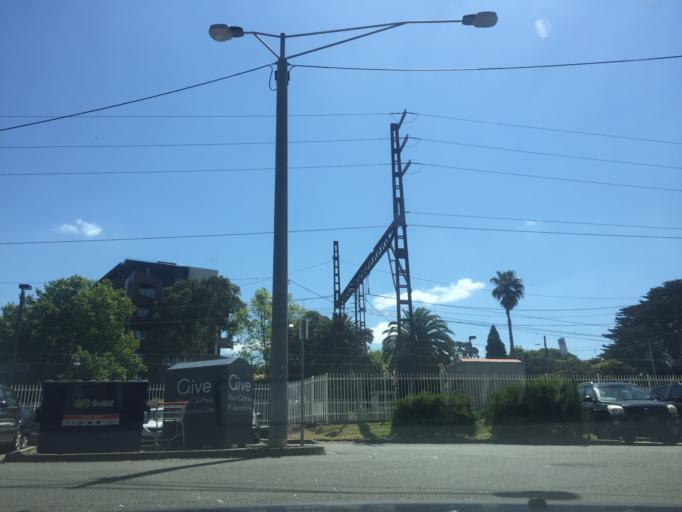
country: AU
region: Victoria
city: Ivanhoe East
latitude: -37.7694
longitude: 145.0449
